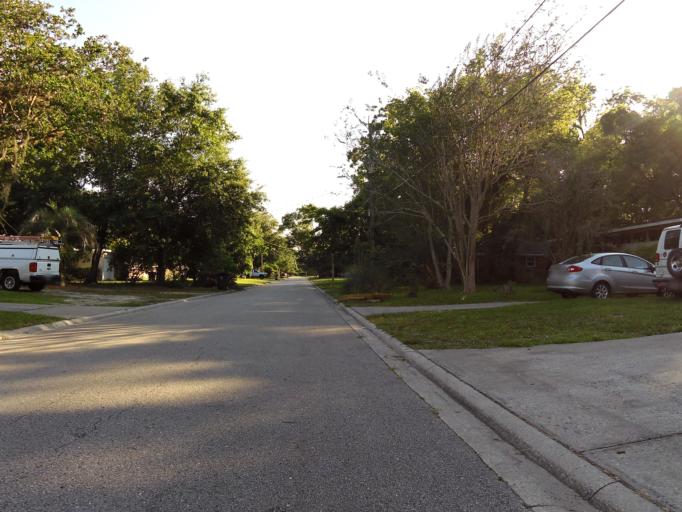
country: US
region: Florida
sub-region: Duval County
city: Jacksonville
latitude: 30.2365
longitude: -81.6136
